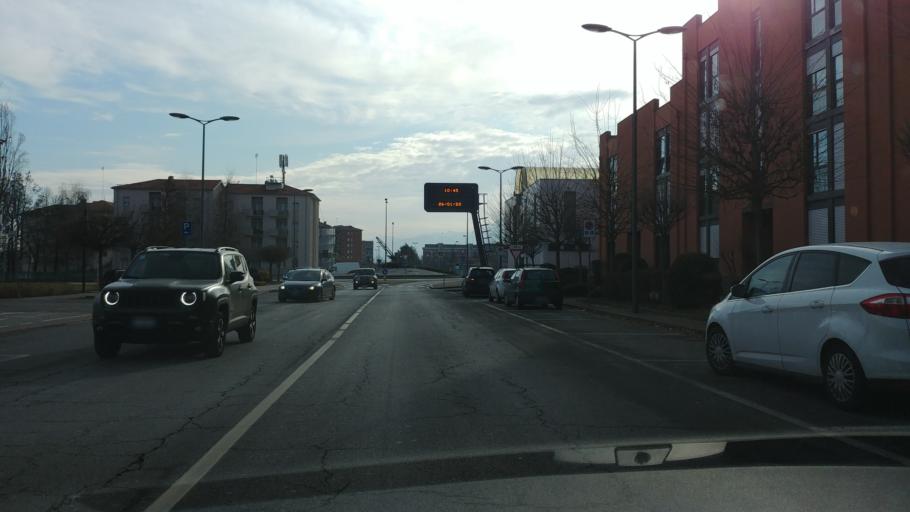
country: IT
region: Piedmont
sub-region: Provincia di Cuneo
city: Cuneo
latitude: 44.3777
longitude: 7.5339
